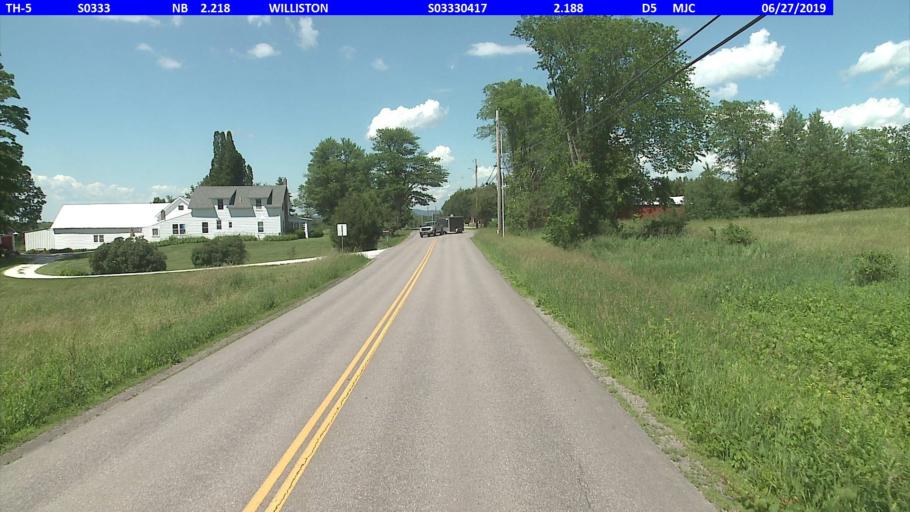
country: US
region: Vermont
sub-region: Chittenden County
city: South Burlington
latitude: 44.4325
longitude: -73.1321
